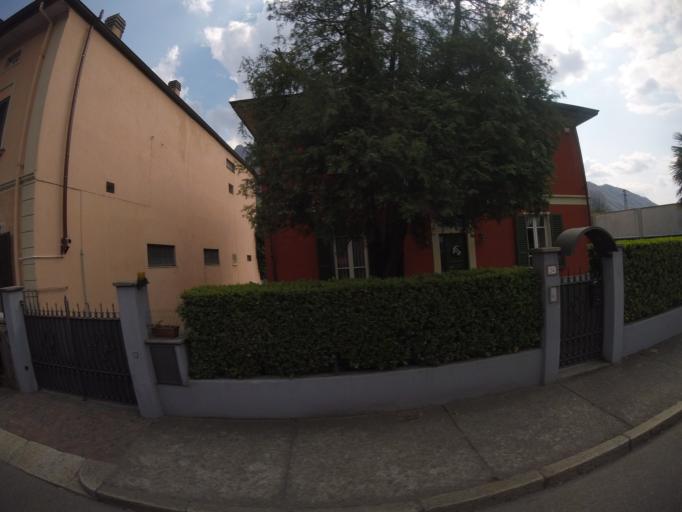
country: IT
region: Piedmont
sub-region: Provincia Verbano-Cusio-Ossola
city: Omegna
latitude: 45.8889
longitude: 8.4091
